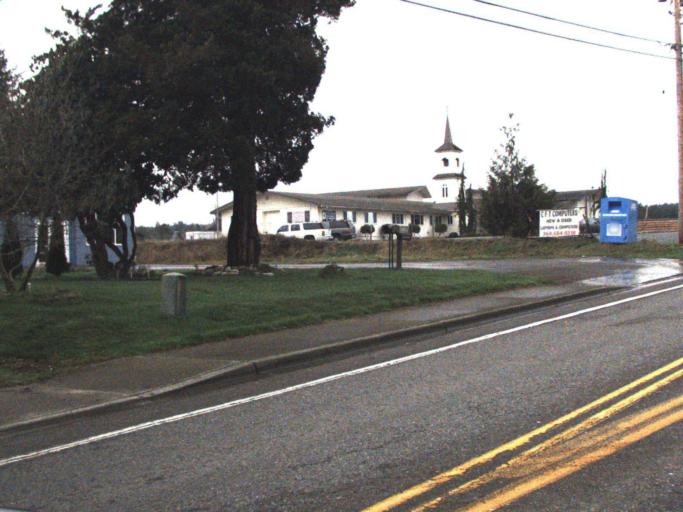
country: US
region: Washington
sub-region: Snohomish County
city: Smokey Point
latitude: 48.1519
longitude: -122.2094
